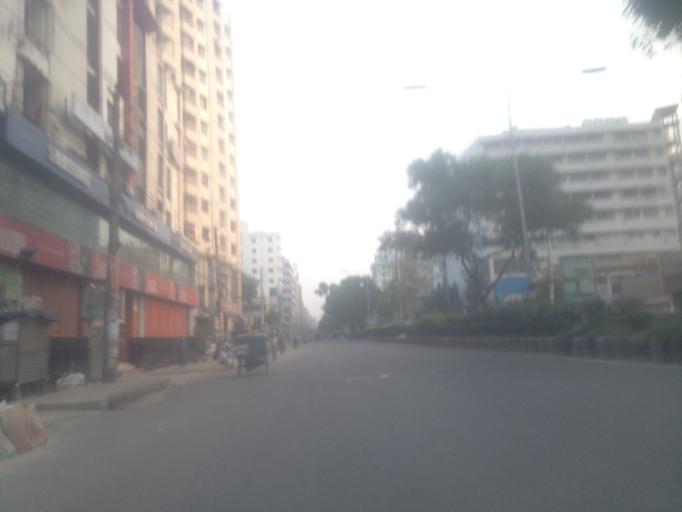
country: BD
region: Dhaka
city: Azimpur
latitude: 23.7875
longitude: 90.3770
